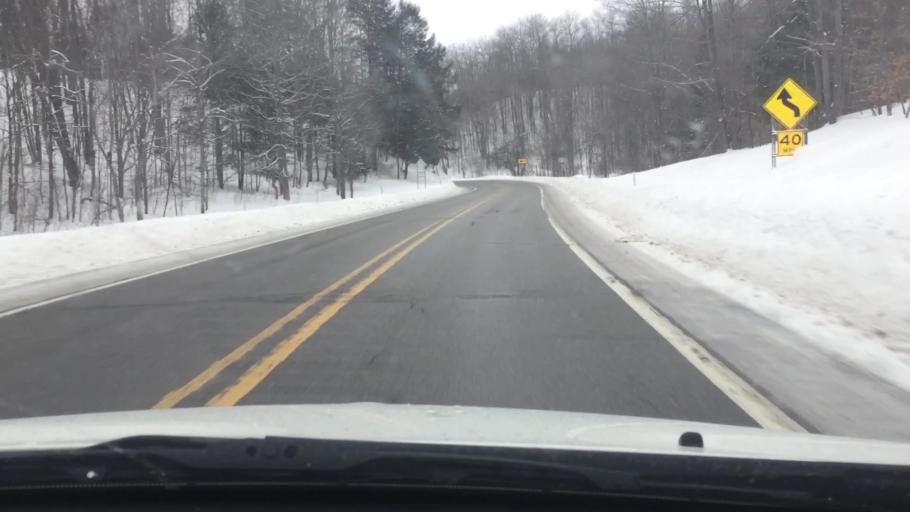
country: US
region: Michigan
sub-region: Charlevoix County
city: Boyne City
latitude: 45.0839
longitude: -84.9319
